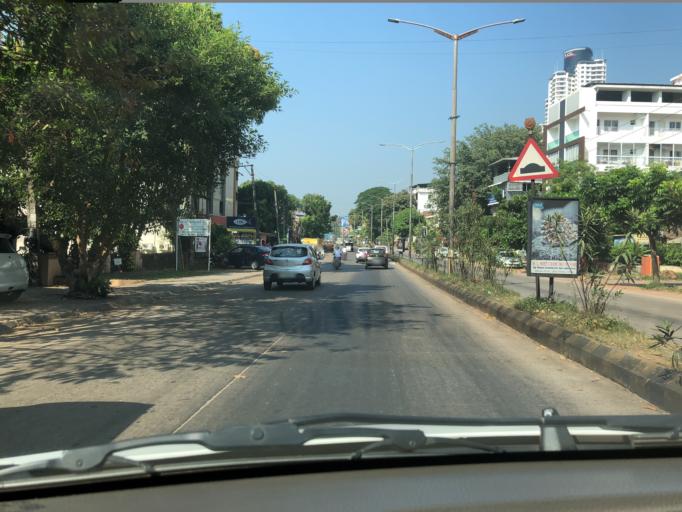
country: IN
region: Karnataka
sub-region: Dakshina Kannada
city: Mangalore
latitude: 12.8910
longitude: 74.8355
